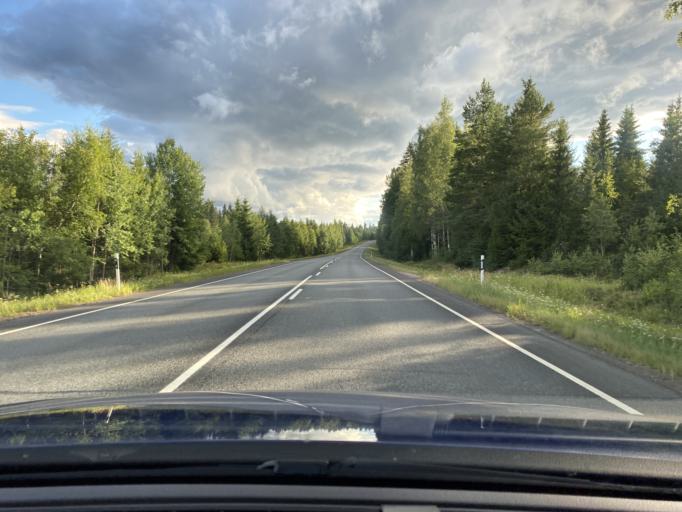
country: FI
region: Haeme
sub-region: Haemeenlinna
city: Renko
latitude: 60.8520
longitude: 24.1557
